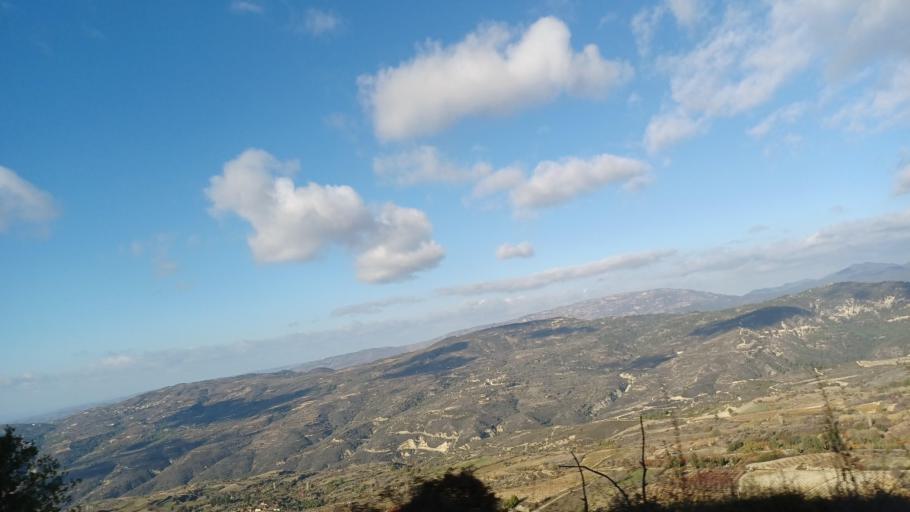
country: CY
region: Limassol
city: Pachna
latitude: 34.8541
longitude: 32.7586
